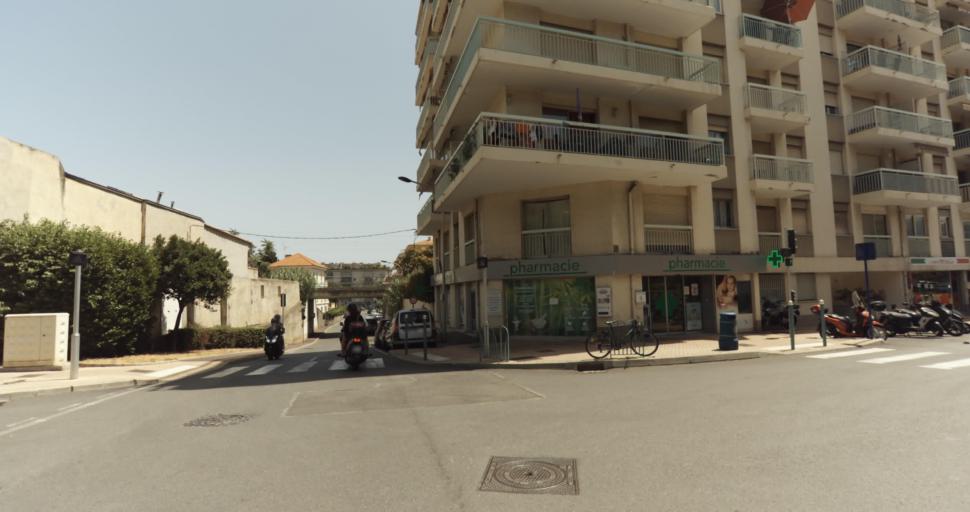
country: FR
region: Provence-Alpes-Cote d'Azur
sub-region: Departement des Alpes-Maritimes
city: Roquebrune-Cap-Martin
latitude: 43.7671
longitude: 7.4856
